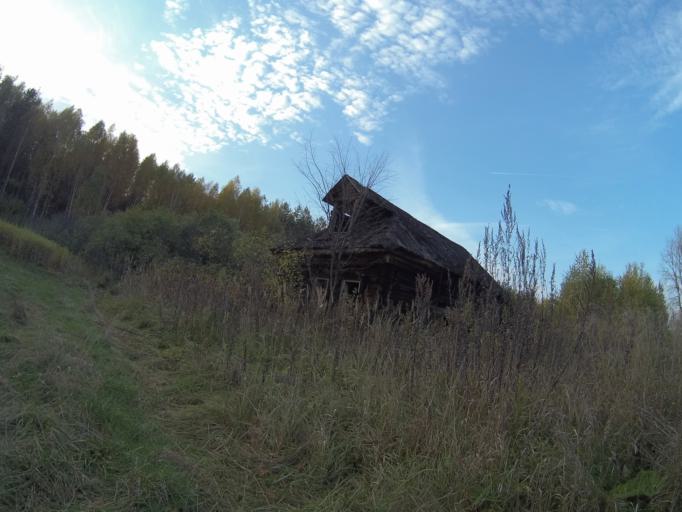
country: RU
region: Vladimir
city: Sobinka
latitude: 55.8303
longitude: 40.0684
